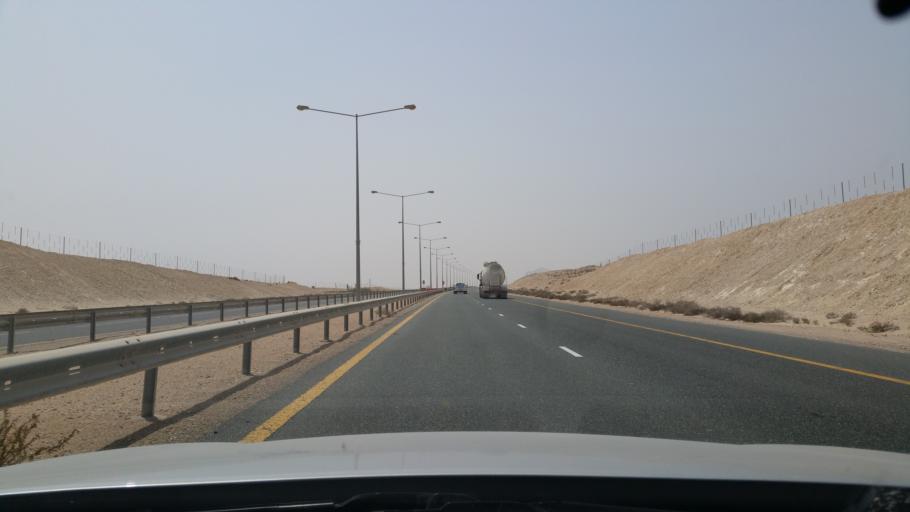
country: QA
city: Umm Bab
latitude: 25.2489
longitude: 50.7989
